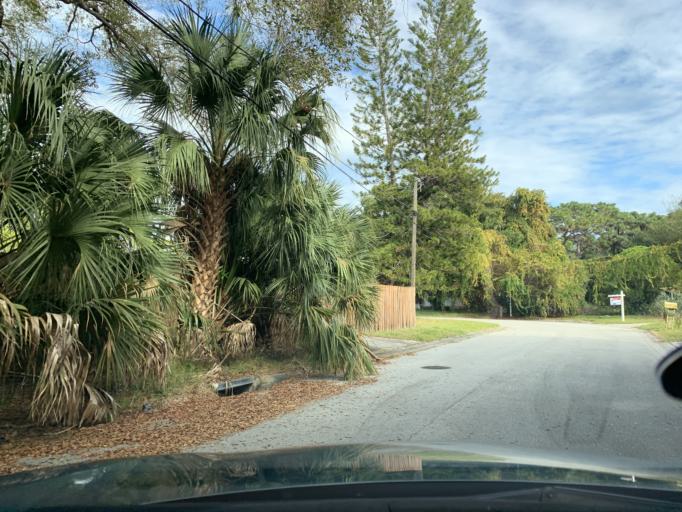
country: US
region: Florida
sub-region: Pinellas County
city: Kenneth City
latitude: 27.8186
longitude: -82.7347
